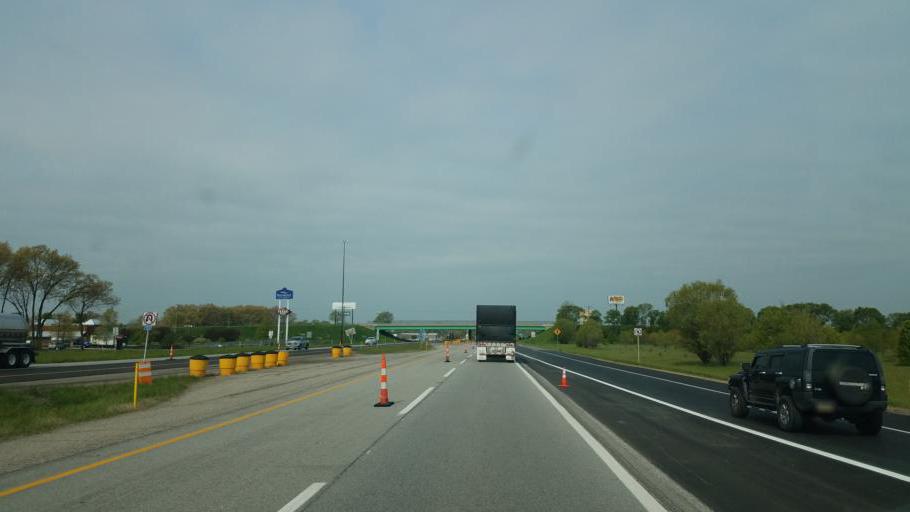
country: US
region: Indiana
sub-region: Elkhart County
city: Simonton Lake
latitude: 41.7310
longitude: -85.9697
